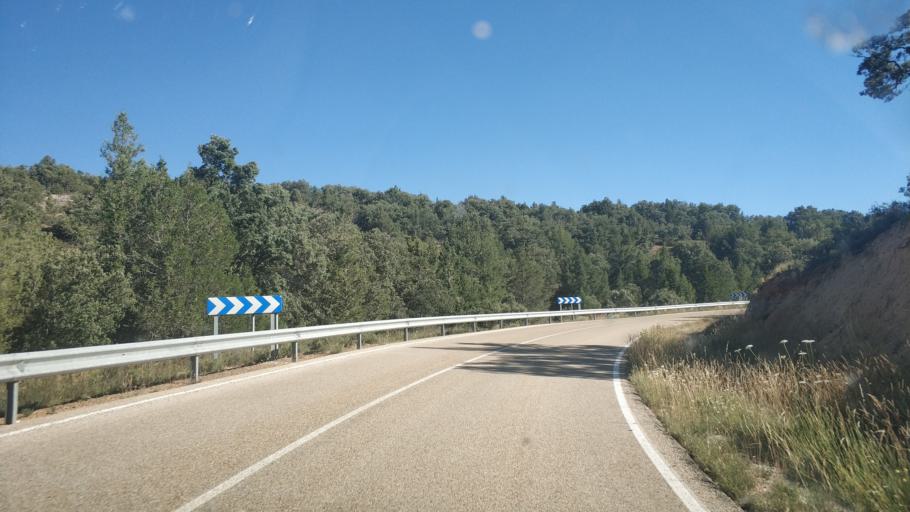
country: ES
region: Castille and Leon
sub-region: Provincia de Soria
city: Montejo de Tiermes
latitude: 41.4252
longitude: -3.2019
